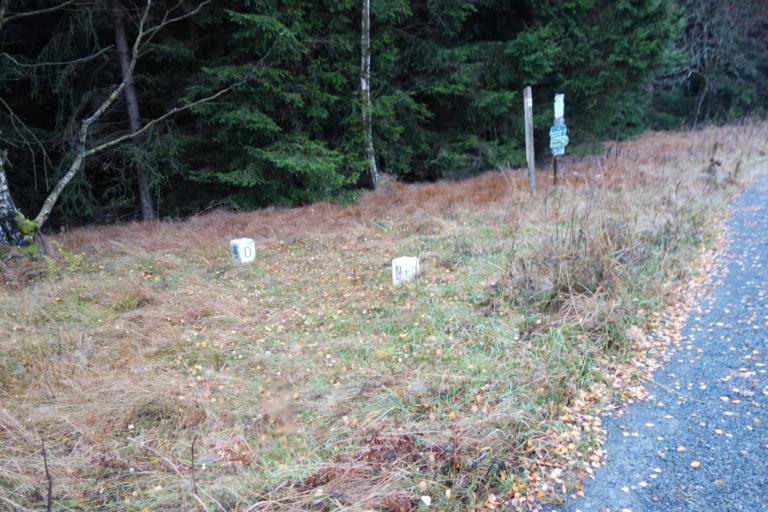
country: DE
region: Saxony
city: Johstadt
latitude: 50.5010
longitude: 13.0716
